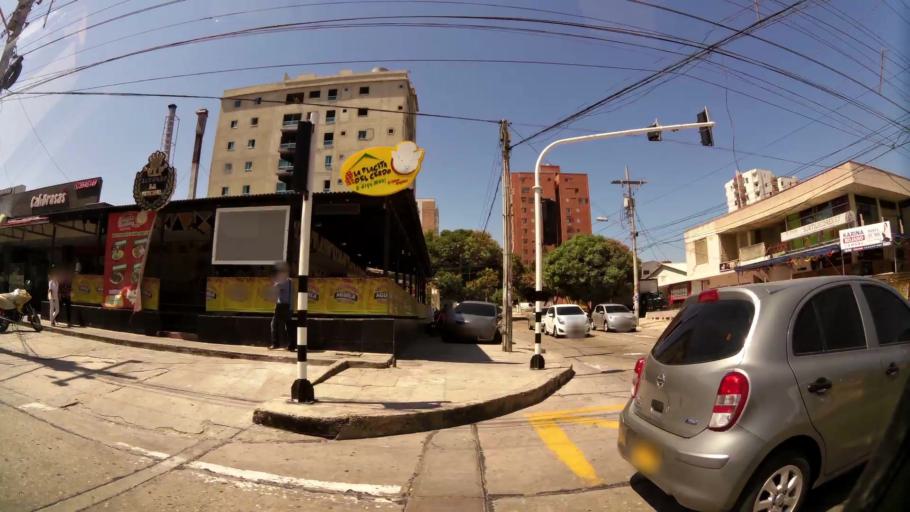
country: CO
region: Atlantico
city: Barranquilla
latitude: 11.0000
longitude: -74.8196
